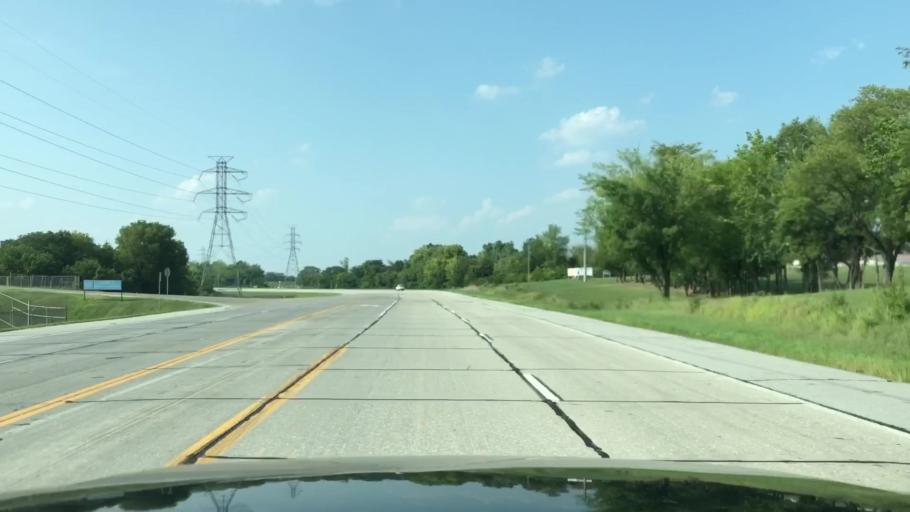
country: US
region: Missouri
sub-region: Saint Charles County
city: Lake Saint Louis
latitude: 38.8161
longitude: -90.8116
